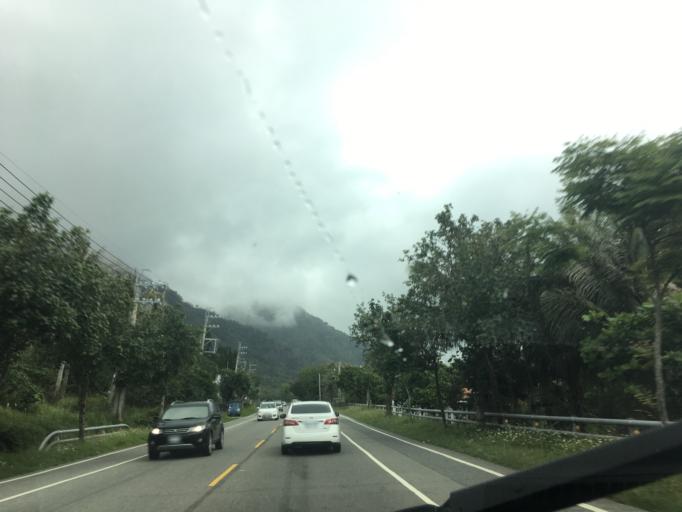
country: TW
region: Taiwan
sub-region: Taitung
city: Taitung
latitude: 22.9381
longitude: 121.2769
